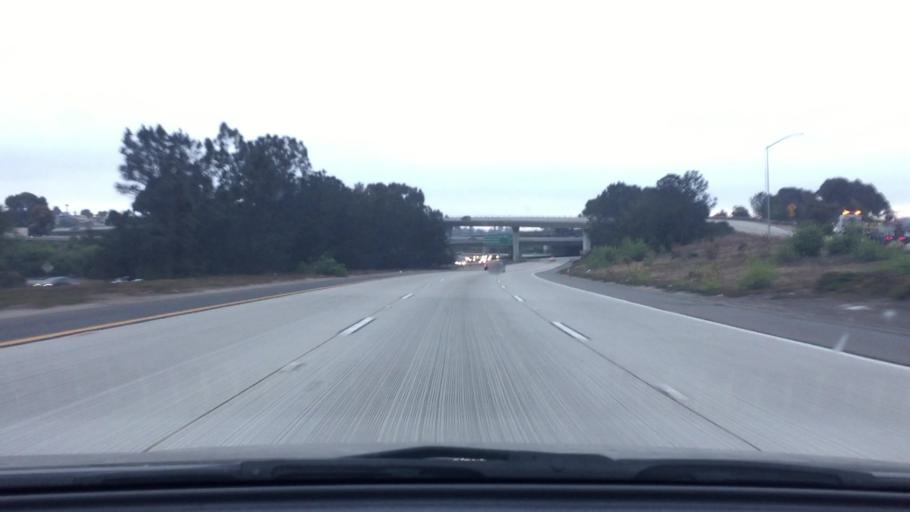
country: US
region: California
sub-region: San Diego County
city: Chula Vista
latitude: 32.6582
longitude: -117.0791
